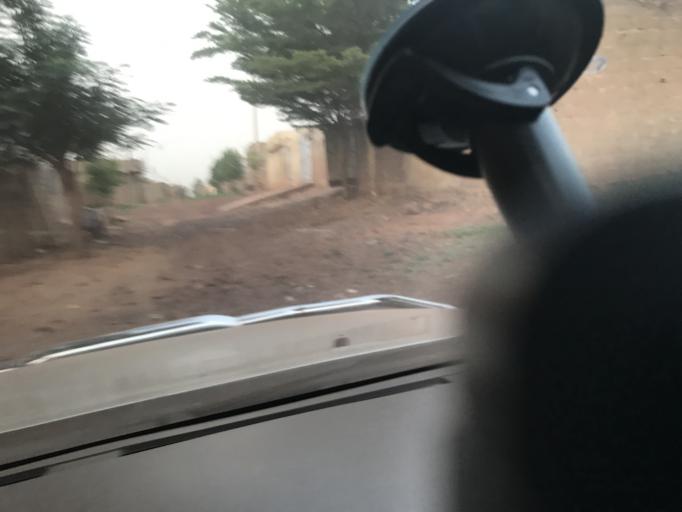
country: ML
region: Bamako
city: Bamako
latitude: 12.6495
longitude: -7.8794
